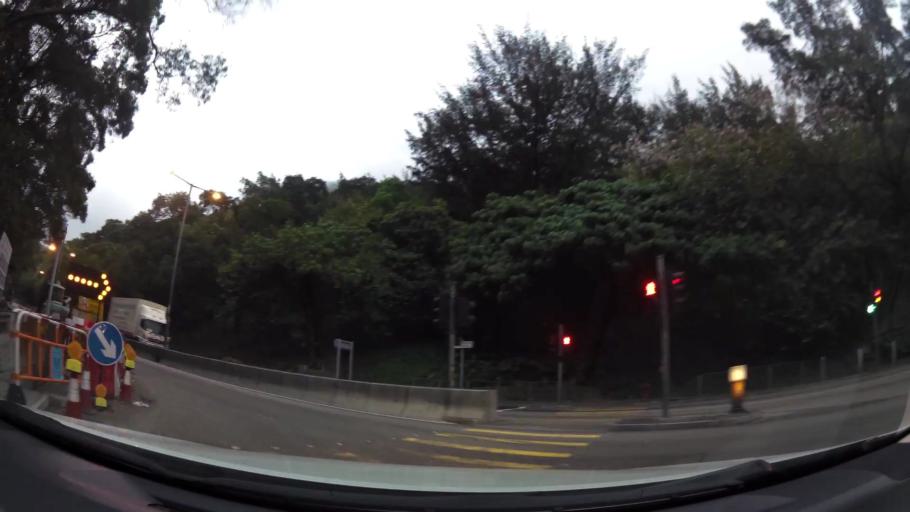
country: HK
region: Tsuen Wan
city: Tsuen Wan
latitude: 22.3389
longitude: 114.0951
